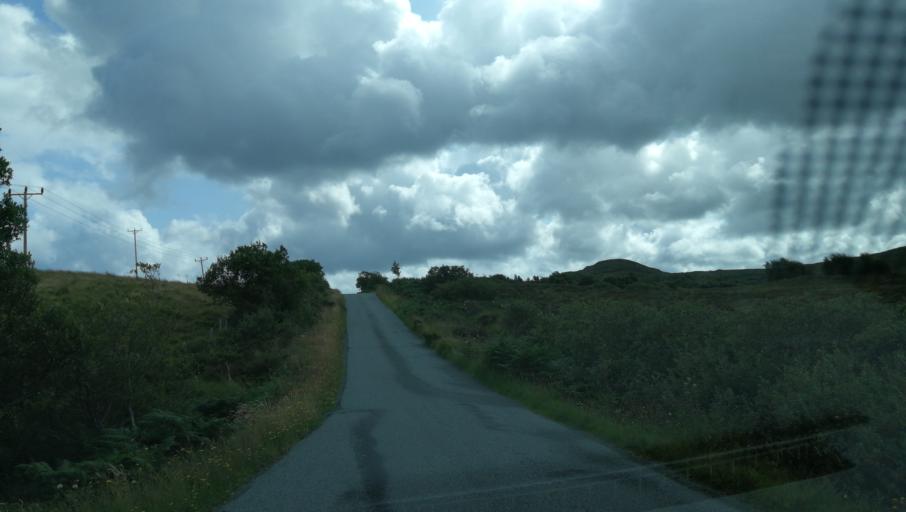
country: GB
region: Scotland
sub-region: Highland
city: Portree
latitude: 57.3818
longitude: -6.1737
